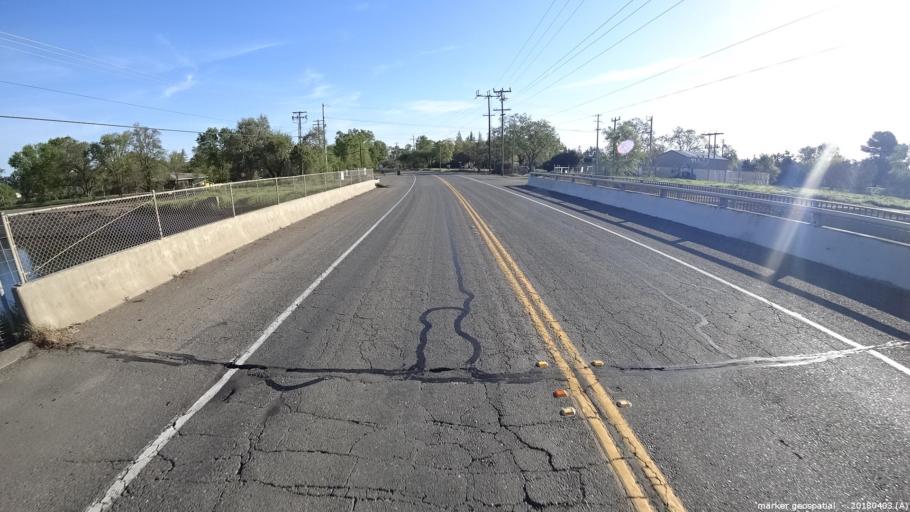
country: US
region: California
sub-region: Sacramento County
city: Wilton
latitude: 38.4425
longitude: -121.1892
